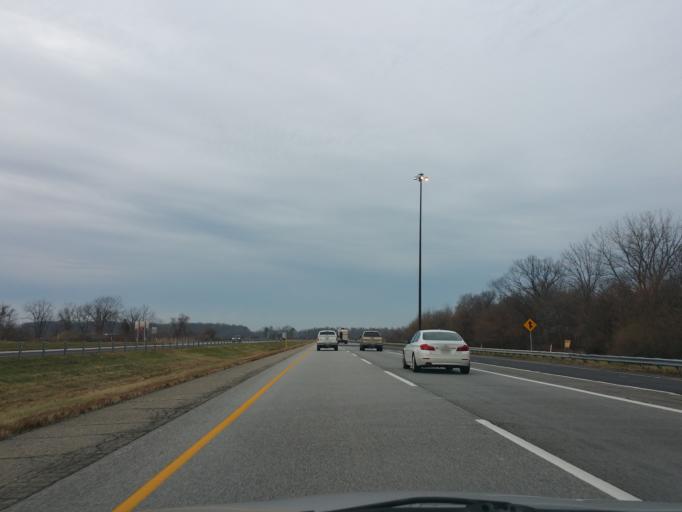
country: US
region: Indiana
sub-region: Porter County
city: Chesterton
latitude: 41.5745
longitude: -87.0530
